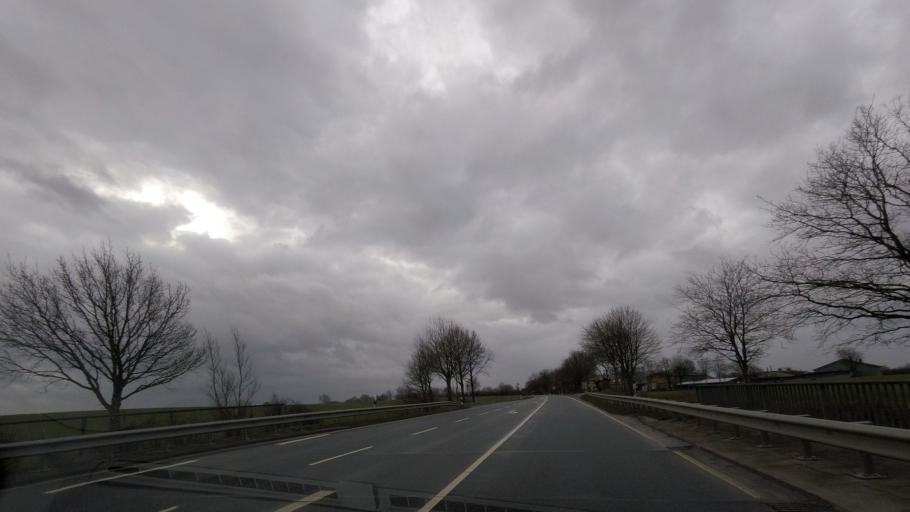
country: DE
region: Schleswig-Holstein
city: Tolk
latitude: 54.5752
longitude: 9.6492
